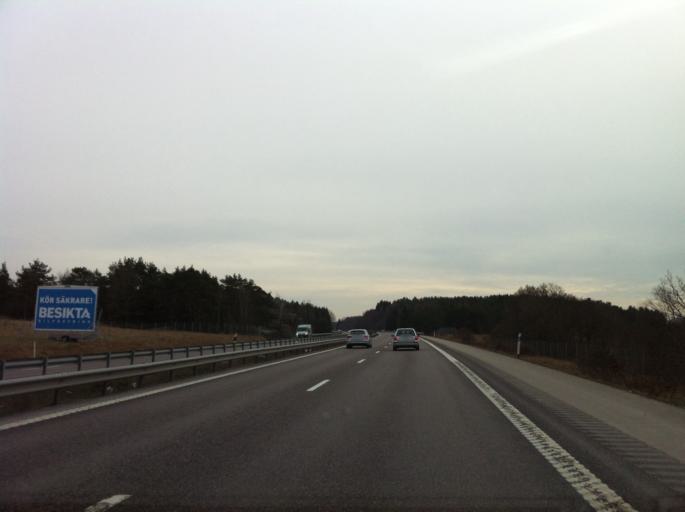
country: SE
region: Vaestra Goetaland
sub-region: Stenungsunds Kommun
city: Stora Hoga
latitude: 58.0218
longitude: 11.8446
